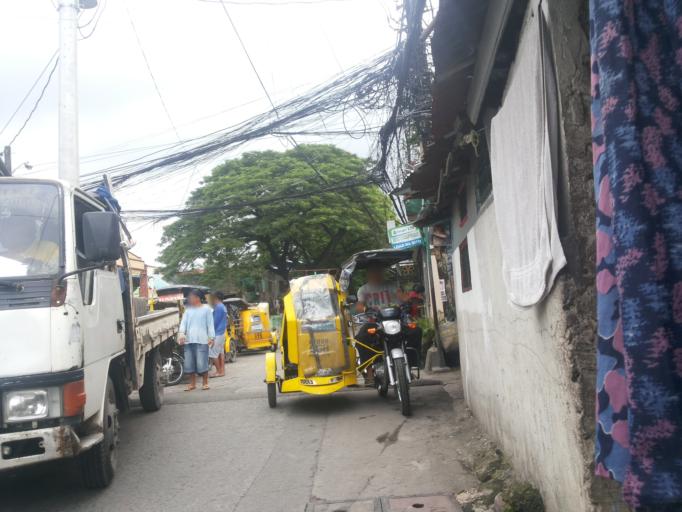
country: PH
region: Calabarzon
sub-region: Province of Rizal
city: Pateros
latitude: 14.5547
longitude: 121.0871
